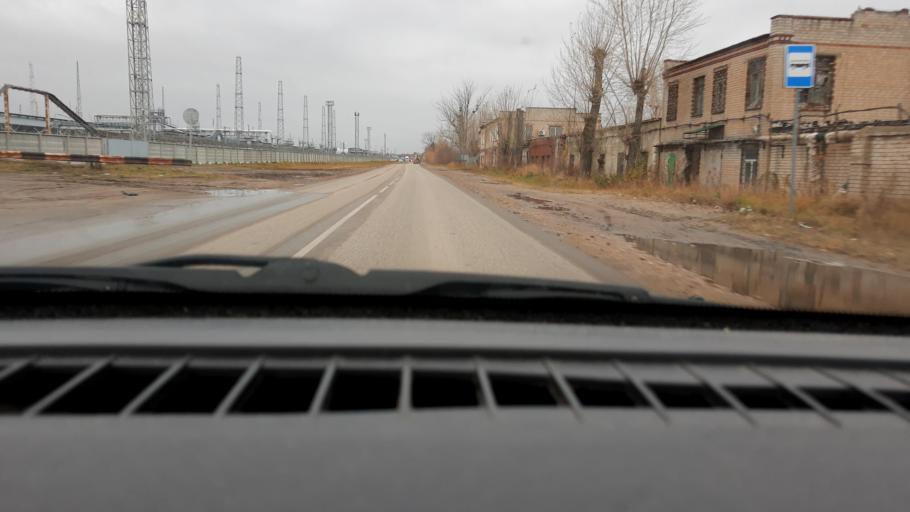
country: RU
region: Nizjnij Novgorod
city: Kstovo
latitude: 56.1191
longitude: 44.1439
